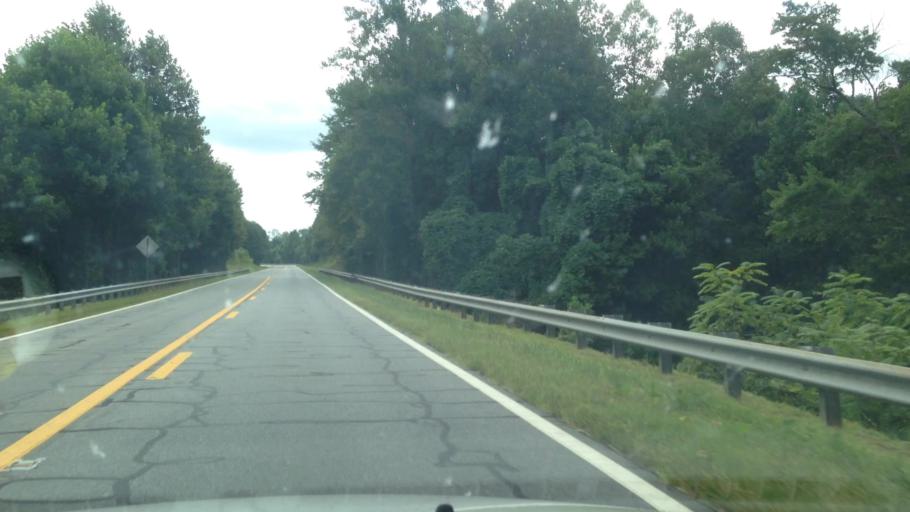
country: US
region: North Carolina
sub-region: Rockingham County
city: Wentworth
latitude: 36.3885
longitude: -79.8163
